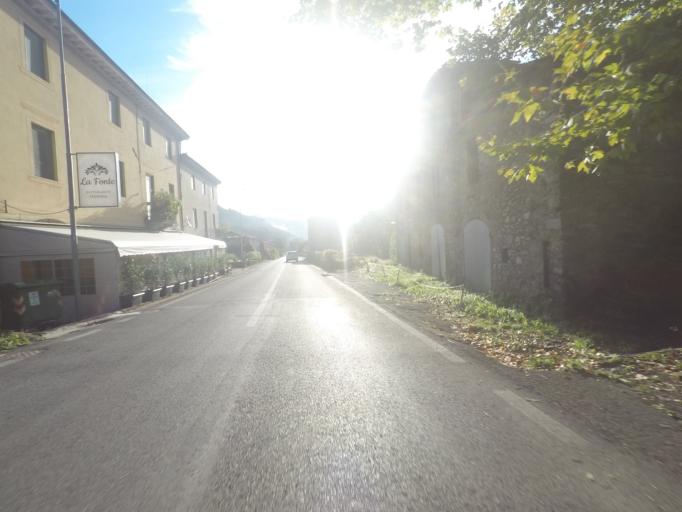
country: IT
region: Tuscany
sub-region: Provincia di Lucca
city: Pescaglia
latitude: 43.9522
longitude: 10.4243
